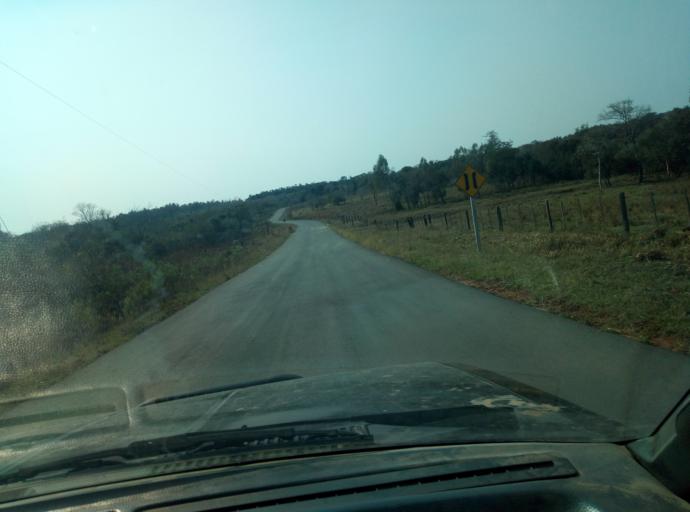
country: PY
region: Caaguazu
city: Carayao
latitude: -25.2637
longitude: -56.2863
